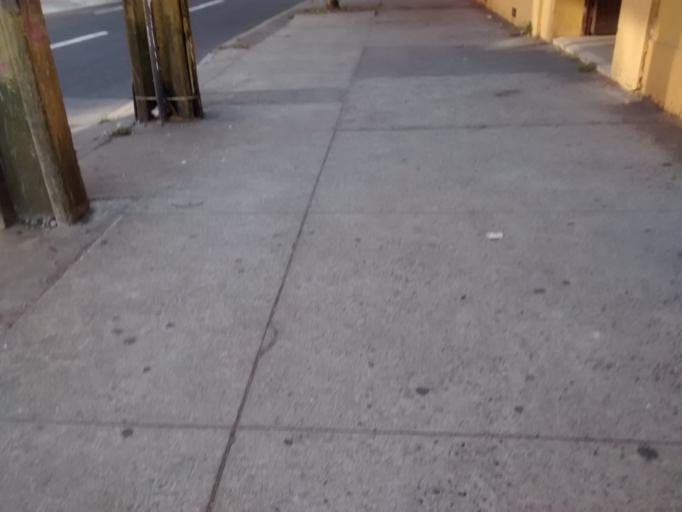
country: CL
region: Biobio
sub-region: Provincia de Concepcion
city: Concepcion
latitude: -36.8307
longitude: -73.0504
